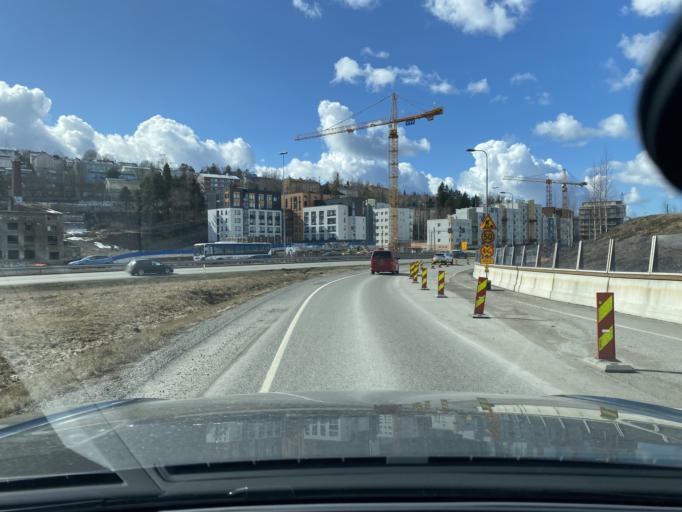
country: FI
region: Pirkanmaa
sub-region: Tampere
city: Tampere
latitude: 61.5043
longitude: 23.7232
